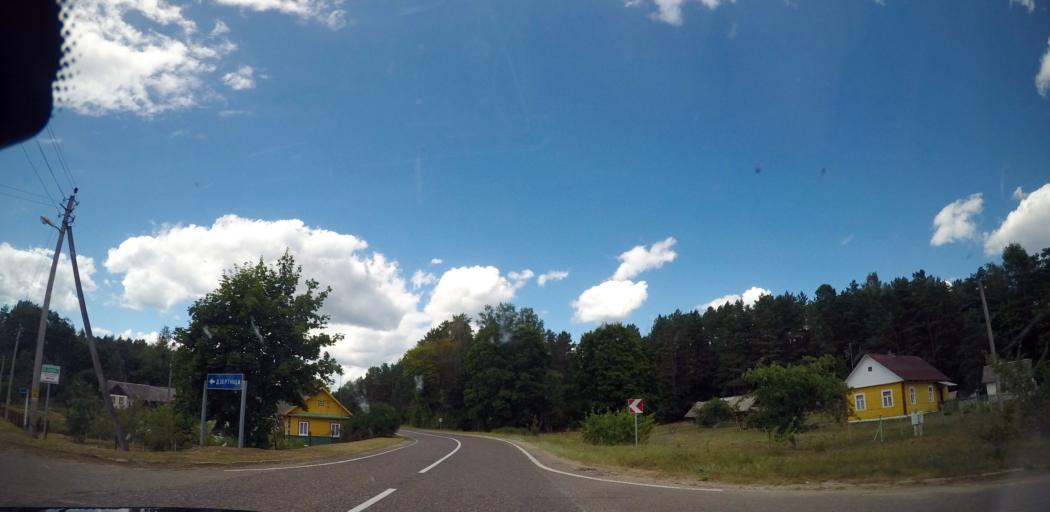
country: BY
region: Grodnenskaya
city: Skidal'
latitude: 53.8231
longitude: 24.2417
